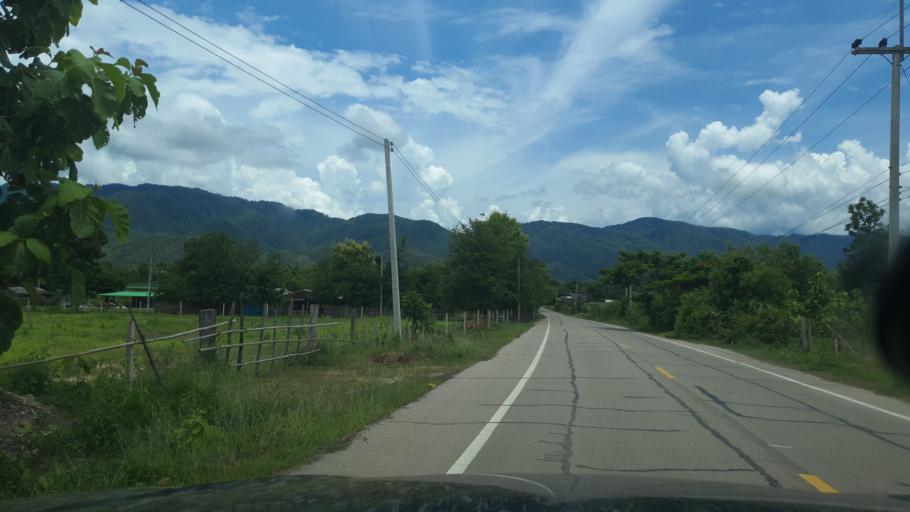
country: TH
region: Lampang
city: Sop Prap
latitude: 17.9154
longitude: 99.4116
